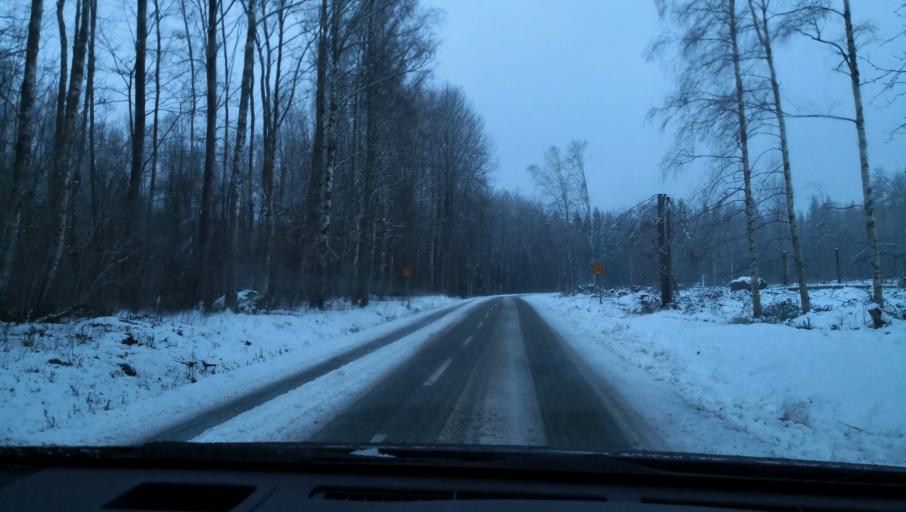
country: SE
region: Vaestmanland
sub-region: Kopings Kommun
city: Kolsva
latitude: 59.5964
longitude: 15.8258
